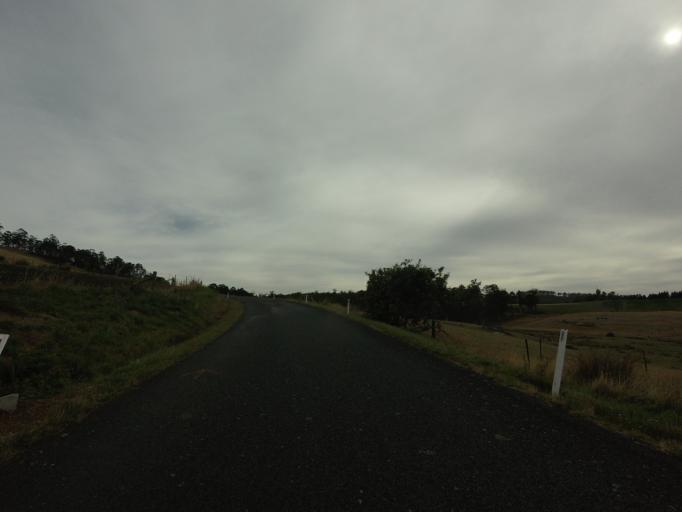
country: AU
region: Tasmania
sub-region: Sorell
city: Sorell
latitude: -42.4794
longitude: 147.5749
